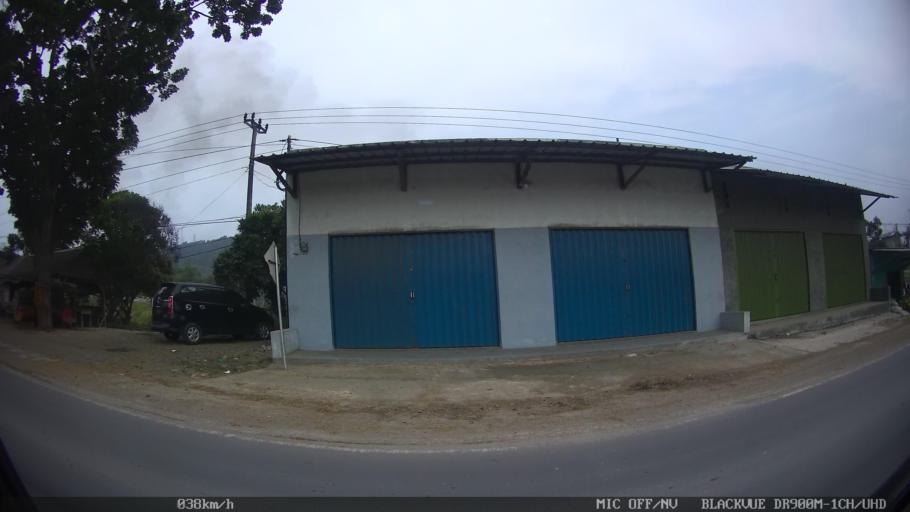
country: ID
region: Lampung
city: Panjang
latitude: -5.4308
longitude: 105.3260
